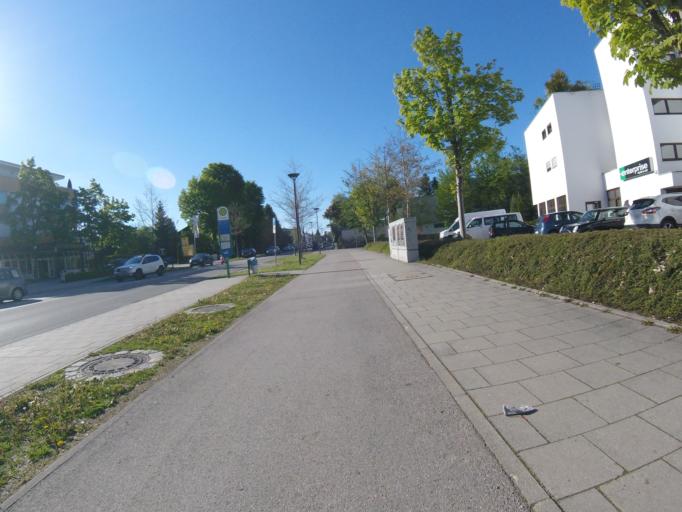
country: DE
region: Bavaria
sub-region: Upper Bavaria
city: Ottobrunn
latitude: 48.0589
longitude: 11.6653
